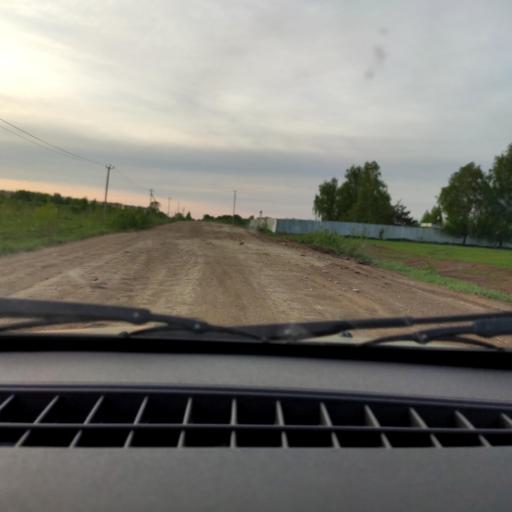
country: RU
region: Bashkortostan
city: Iglino
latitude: 54.8493
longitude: 56.4005
